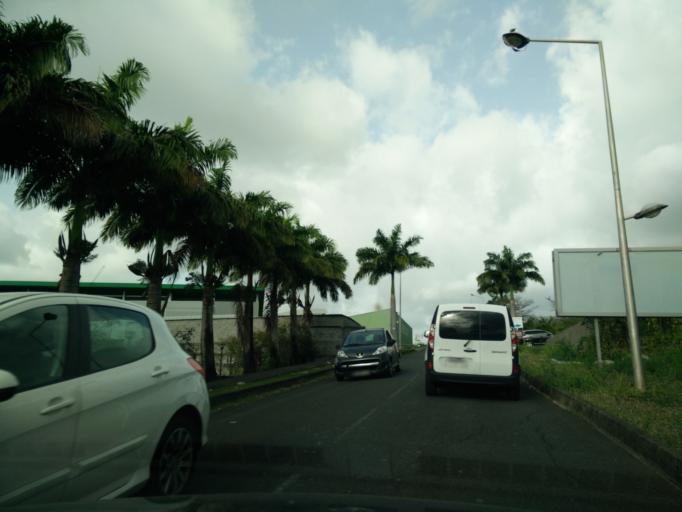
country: GP
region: Guadeloupe
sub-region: Guadeloupe
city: Baie-Mahault
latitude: 16.2385
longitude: -61.5730
